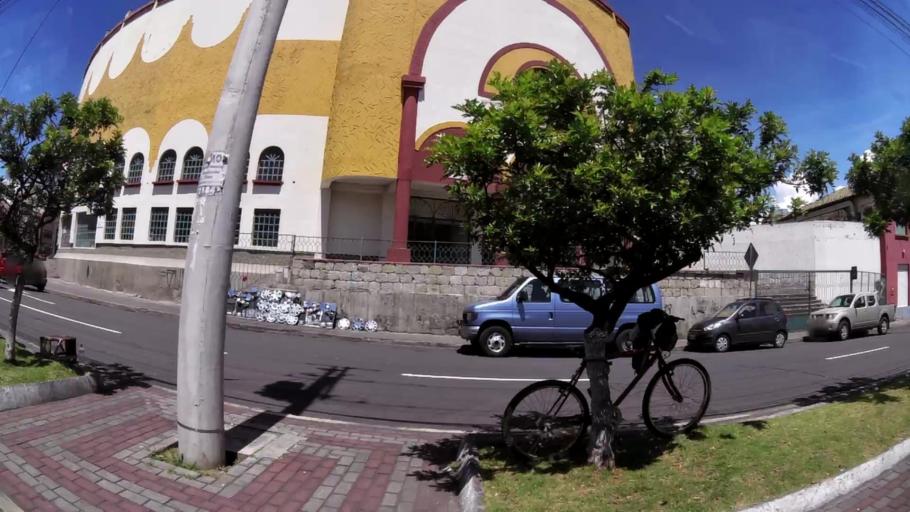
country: EC
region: Chimborazo
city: Riobamba
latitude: -1.6686
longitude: -78.6558
